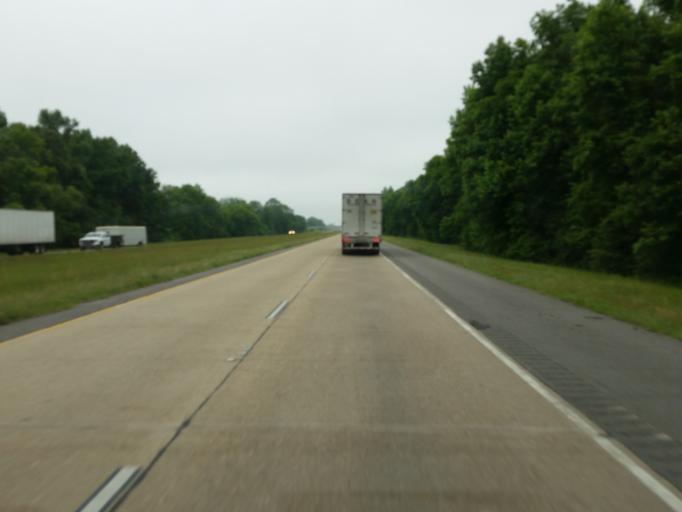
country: US
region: Louisiana
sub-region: Madison Parish
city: Tallulah
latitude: 32.3703
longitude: -91.1405
